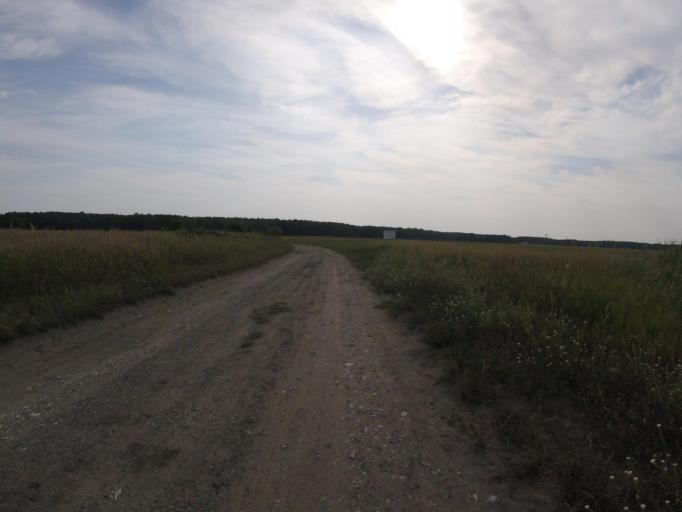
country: DE
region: Brandenburg
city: Spreenhagen
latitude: 52.2820
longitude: 13.8118
